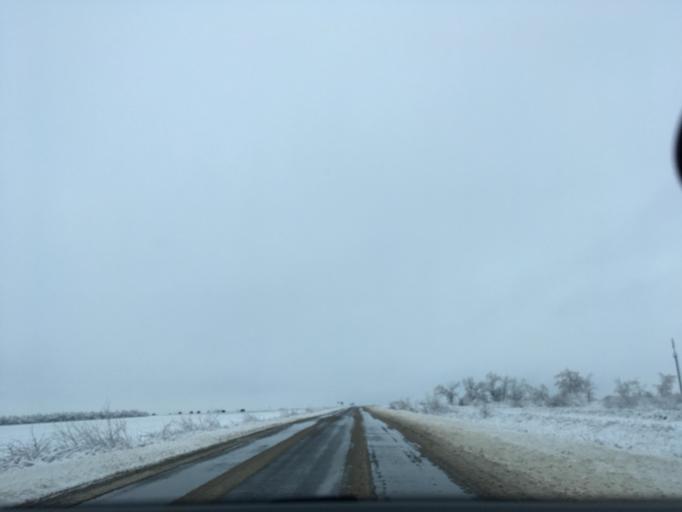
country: RU
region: Voronezj
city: Ol'khovatka
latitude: 50.1268
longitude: 39.1841
